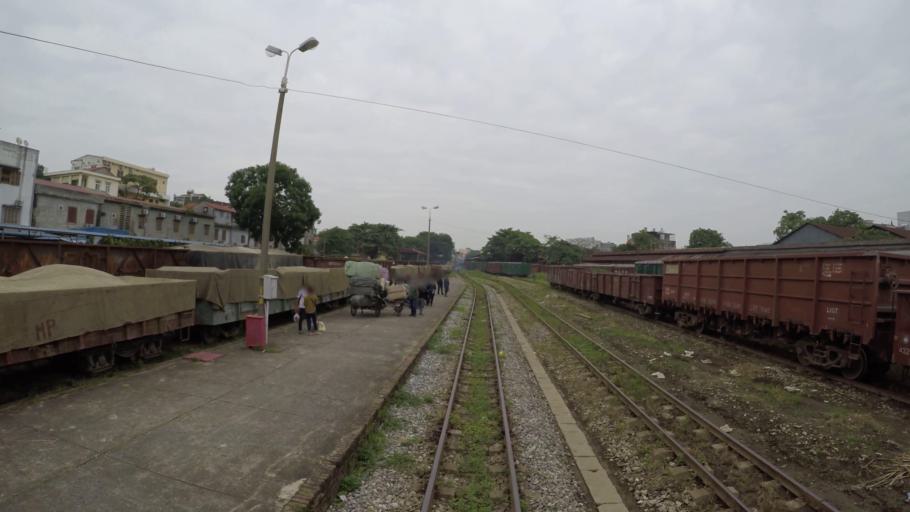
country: VN
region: Hai Phong
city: Haiphong
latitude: 20.8531
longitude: 106.6846
